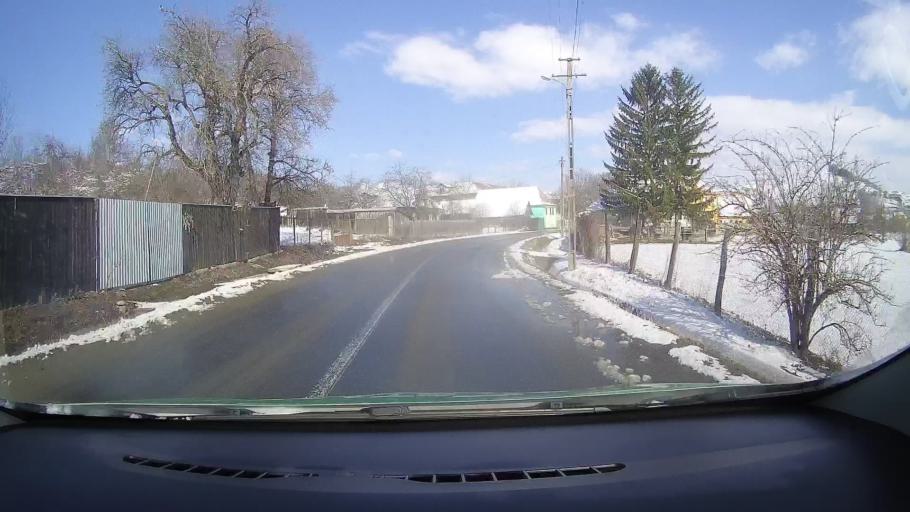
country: RO
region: Sibiu
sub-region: Comuna Barghis
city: Barghis
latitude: 45.9861
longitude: 24.4816
